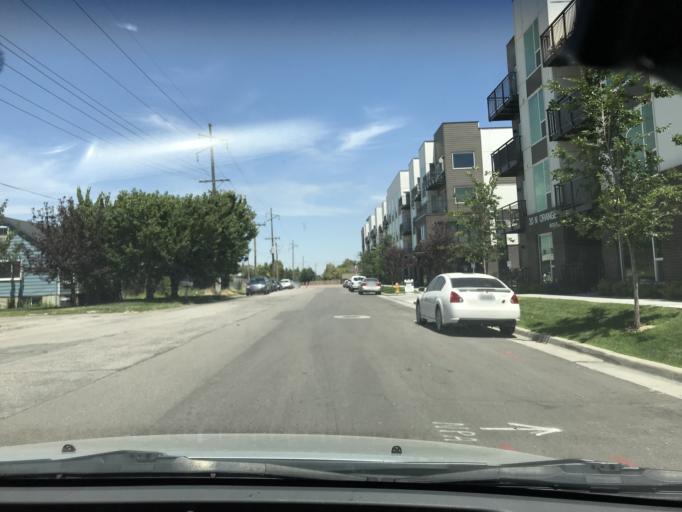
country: US
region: Utah
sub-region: Salt Lake County
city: Salt Lake City
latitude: 40.7700
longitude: -111.9439
